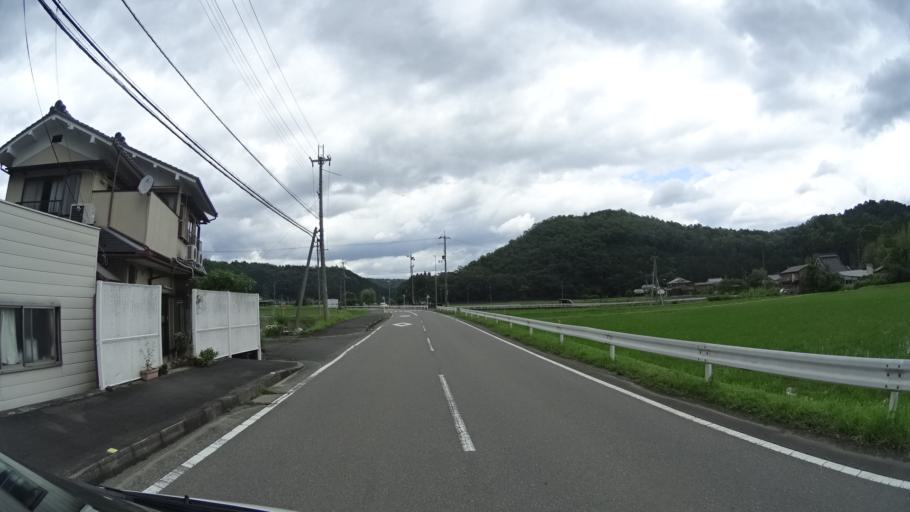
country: JP
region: Kyoto
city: Kameoka
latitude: 35.1004
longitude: 135.4341
